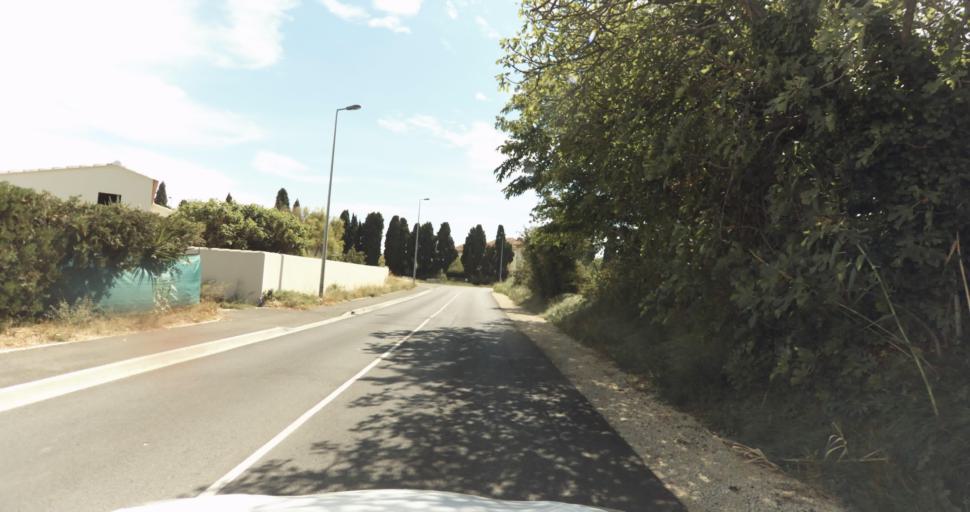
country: FR
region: Provence-Alpes-Cote d'Azur
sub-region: Departement des Bouches-du-Rhone
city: Miramas
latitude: 43.5866
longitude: 4.9957
